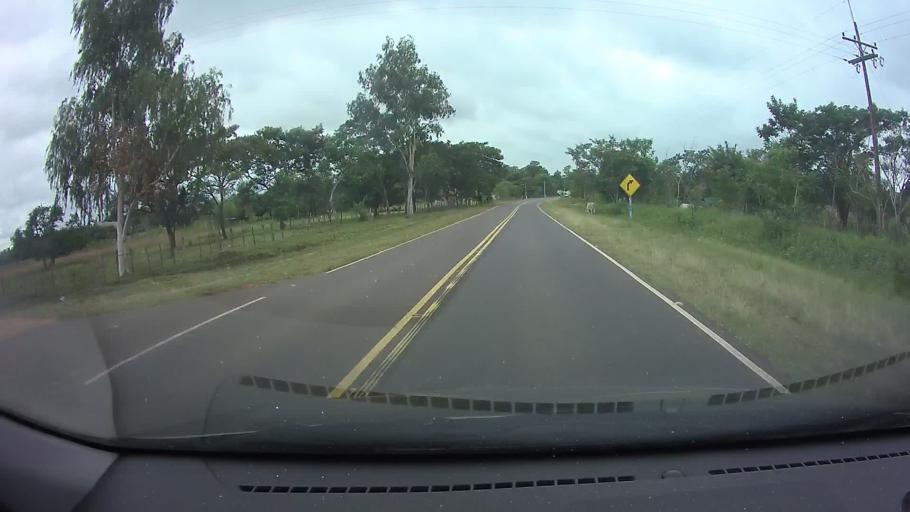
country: PY
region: Central
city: Nueva Italia
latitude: -25.6117
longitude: -57.4423
